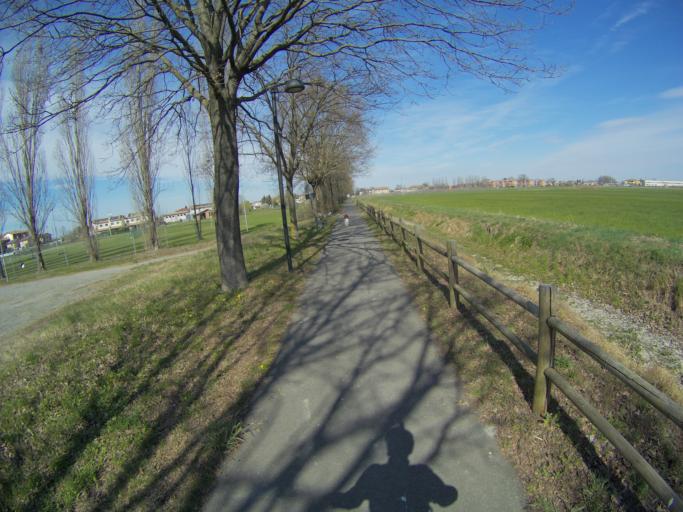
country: IT
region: Emilia-Romagna
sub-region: Provincia di Reggio Emilia
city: Massenzatico
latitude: 44.7052
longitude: 10.6821
